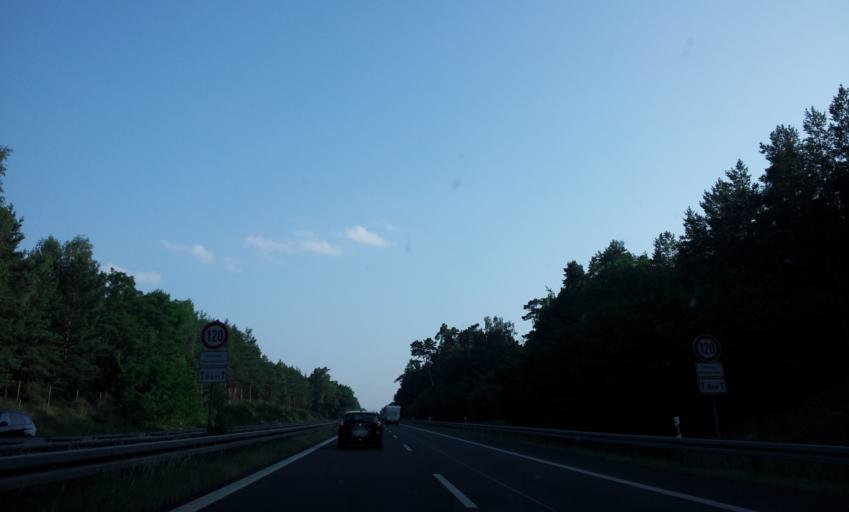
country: DE
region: Brandenburg
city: Althuttendorf
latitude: 53.0320
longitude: 13.8310
